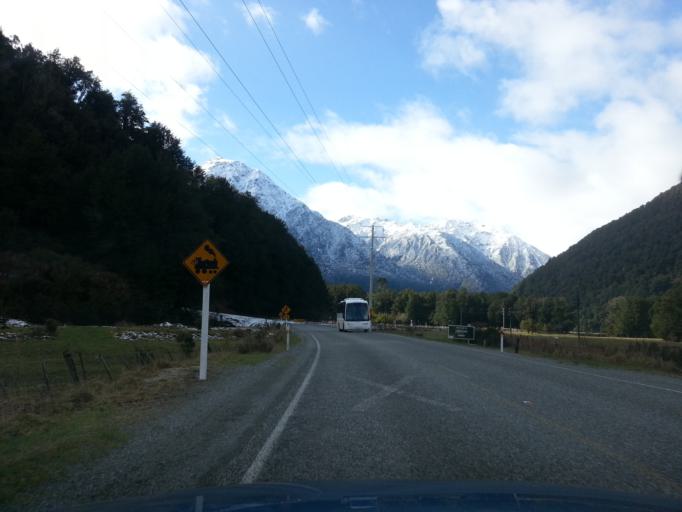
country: NZ
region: West Coast
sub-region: Grey District
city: Greymouth
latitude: -42.7748
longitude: 171.6218
